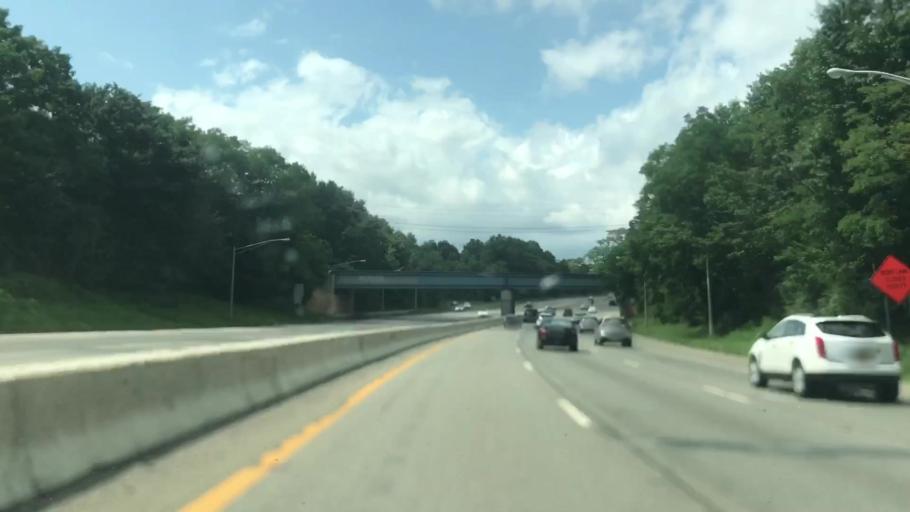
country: US
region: New Jersey
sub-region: Middlesex County
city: Fords
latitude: 40.5219
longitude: -74.2918
